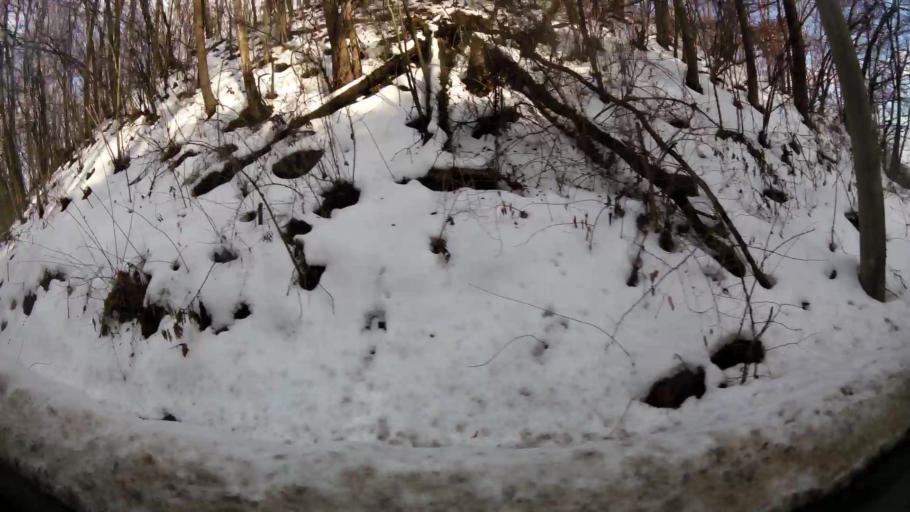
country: BG
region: Sofia-Capital
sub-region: Stolichna Obshtina
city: Sofia
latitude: 42.6457
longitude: 23.2494
